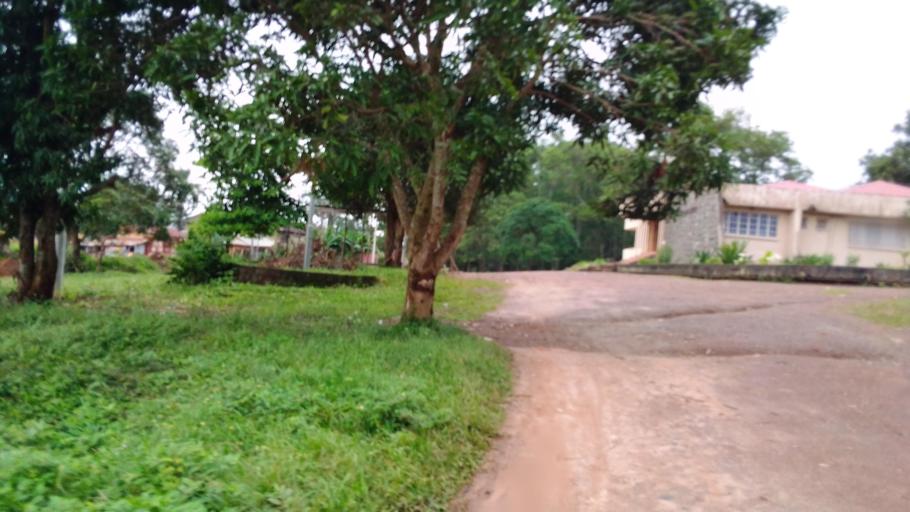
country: SL
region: Eastern Province
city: Kenema
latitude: 7.8818
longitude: -11.1963
